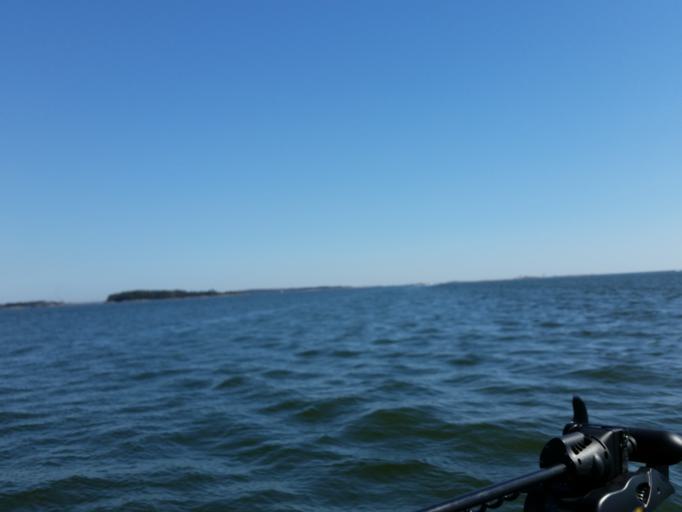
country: FI
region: Uusimaa
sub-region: Helsinki
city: Koukkuniemi
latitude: 60.1438
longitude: 24.7958
